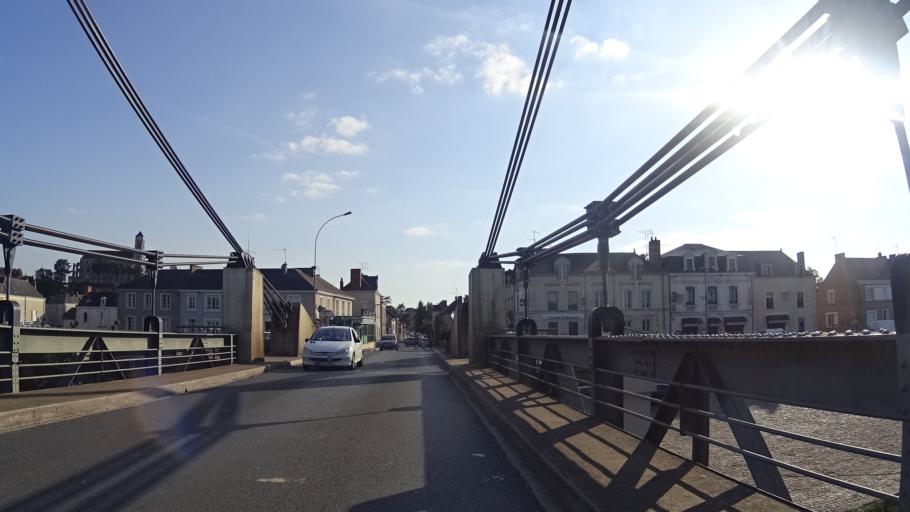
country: FR
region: Pays de la Loire
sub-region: Departement de Maine-et-Loire
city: Montjean-sur-Loire
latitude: 47.3924
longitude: -0.8608
